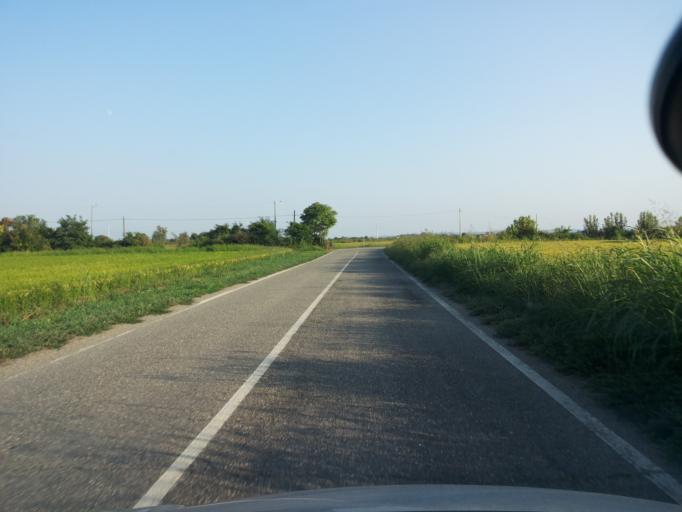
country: IT
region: Piedmont
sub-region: Provincia di Vercelli
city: Lignana
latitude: 45.2965
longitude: 8.3539
